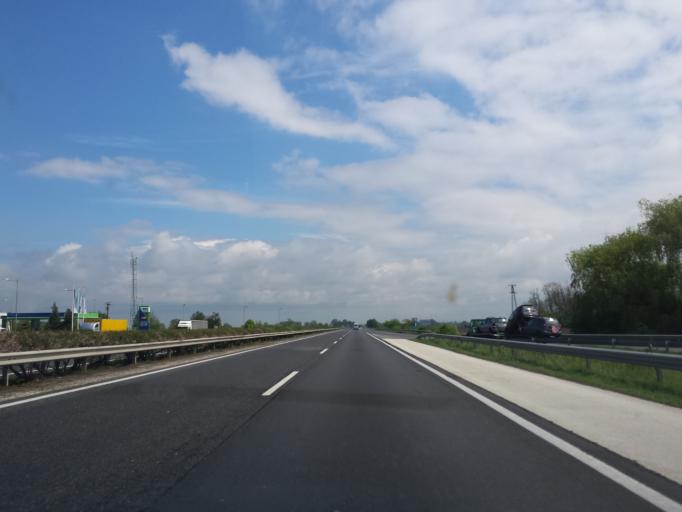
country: HU
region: Komarom-Esztergom
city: Babolna
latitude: 47.6813
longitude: 17.9782
